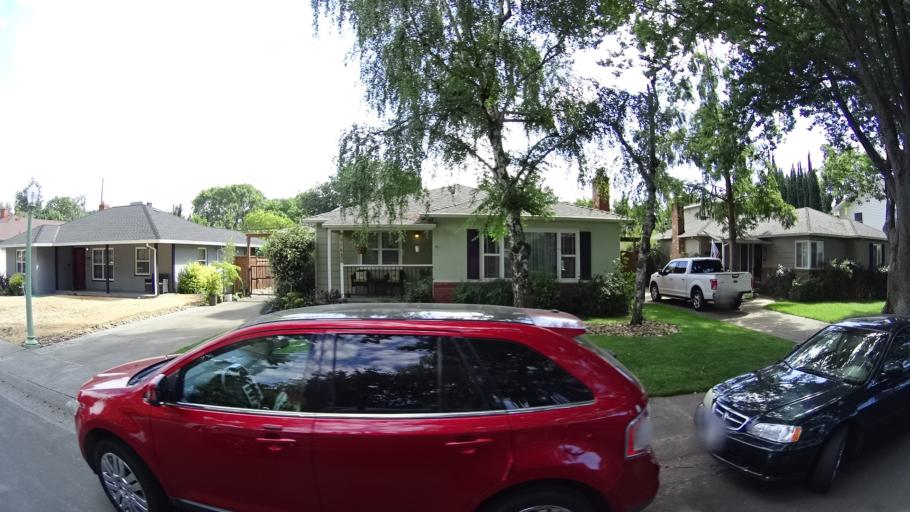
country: US
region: California
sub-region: Sacramento County
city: Arden-Arcade
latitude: 38.5748
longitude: -121.4282
